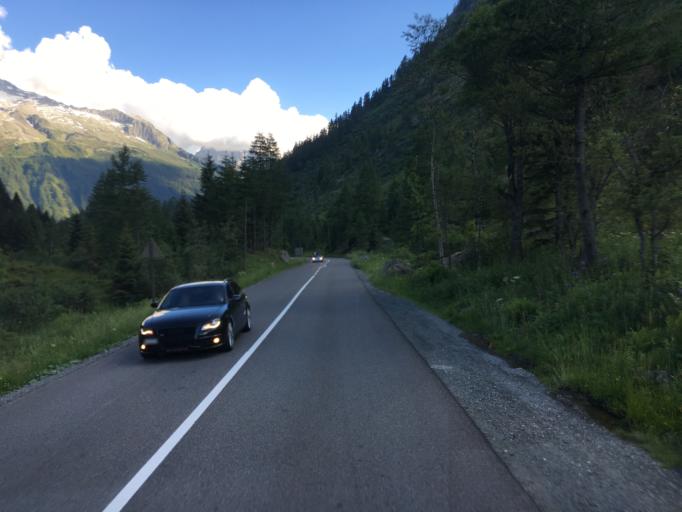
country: FR
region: Rhone-Alpes
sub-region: Departement de la Haute-Savoie
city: Chamonix-Mont-Blanc
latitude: 46.0032
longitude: 6.9235
